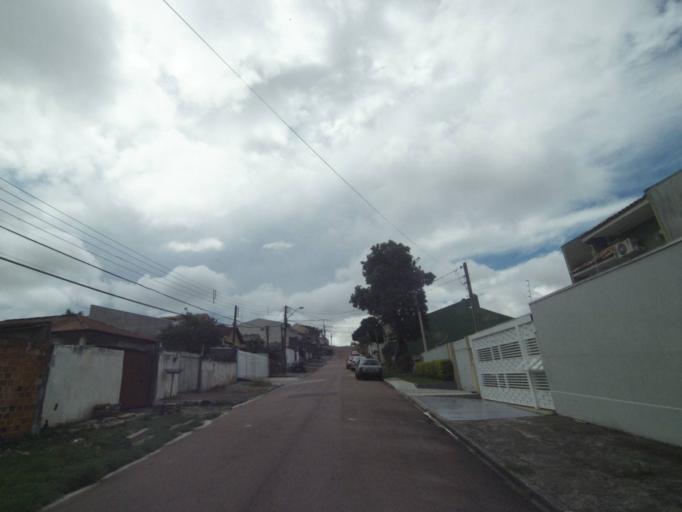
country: BR
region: Parana
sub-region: Curitiba
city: Curitiba
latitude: -25.4834
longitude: -49.2782
